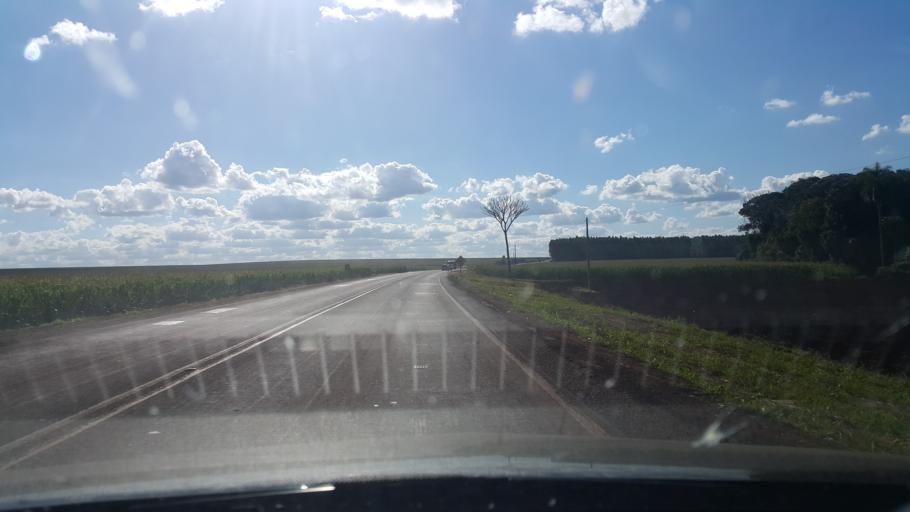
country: BR
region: Mato Grosso do Sul
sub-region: Maracaju
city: Maracaju
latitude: -21.5951
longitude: -55.1949
